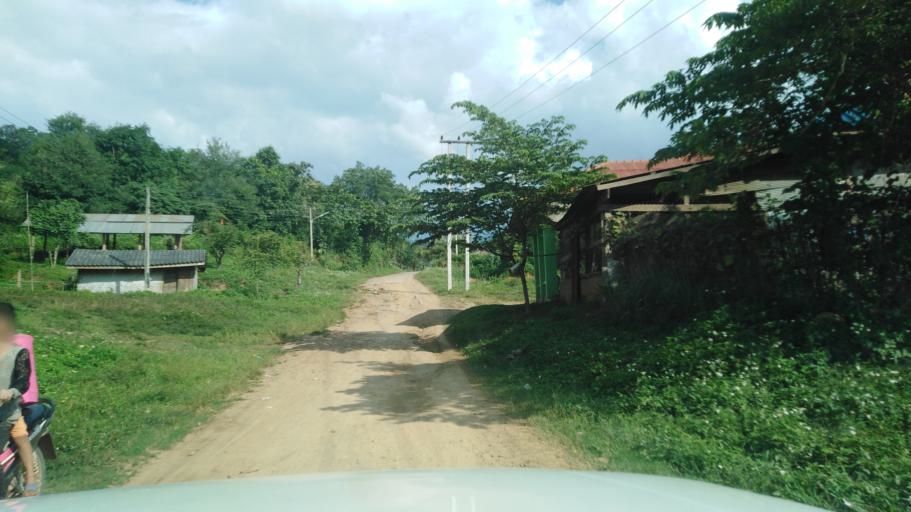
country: TH
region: Chiang Rai
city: Wiang Kaen
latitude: 19.7920
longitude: 100.6161
